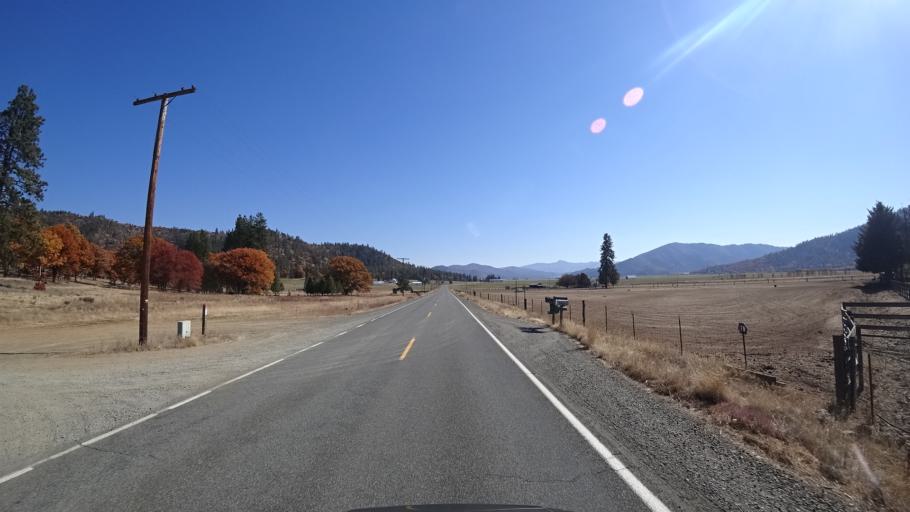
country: US
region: California
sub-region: Siskiyou County
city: Yreka
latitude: 41.6412
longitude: -122.9198
